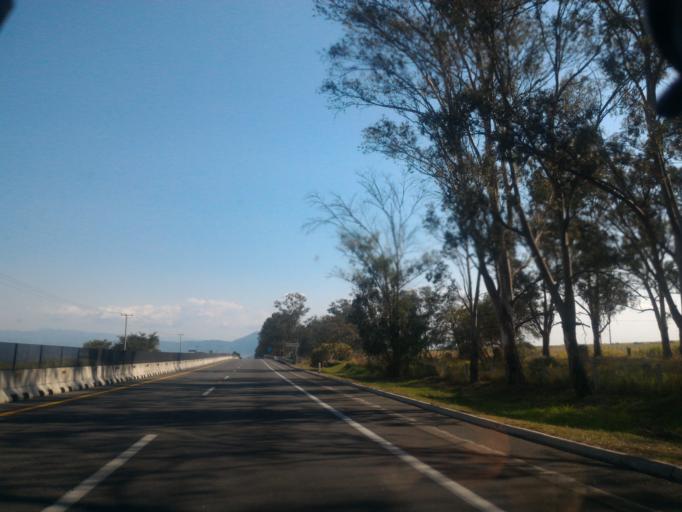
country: MX
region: Jalisco
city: Zapotiltic
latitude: 19.5844
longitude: -103.4492
